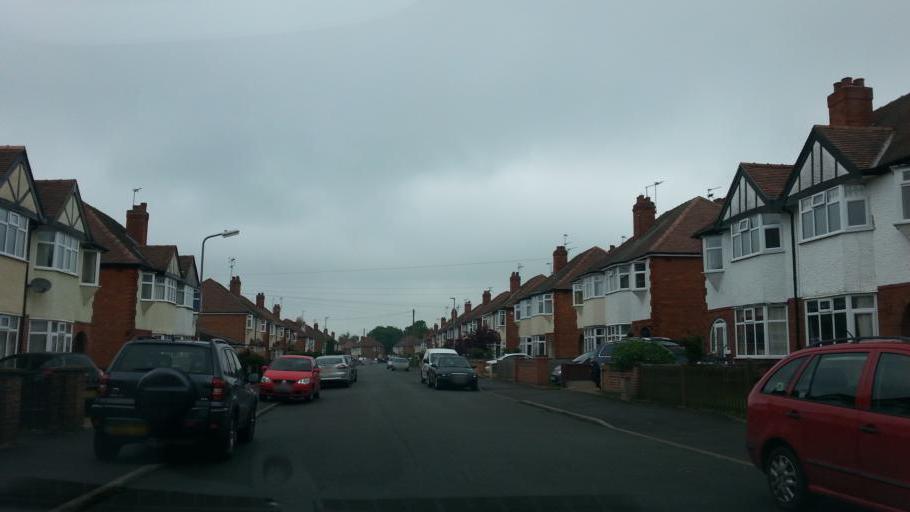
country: GB
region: England
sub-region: Nottinghamshire
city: Newark on Trent
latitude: 53.0645
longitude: -0.7961
